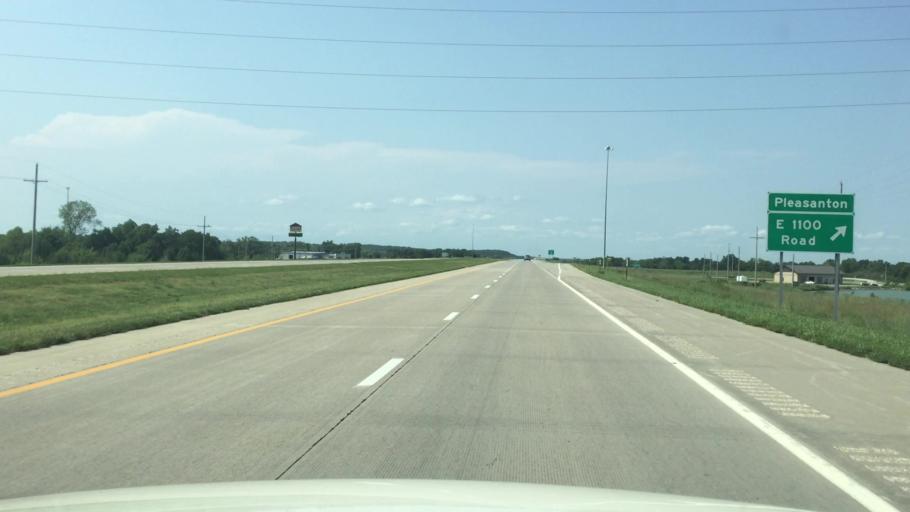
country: US
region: Kansas
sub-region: Linn County
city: Pleasanton
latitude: 38.1776
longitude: -94.6975
